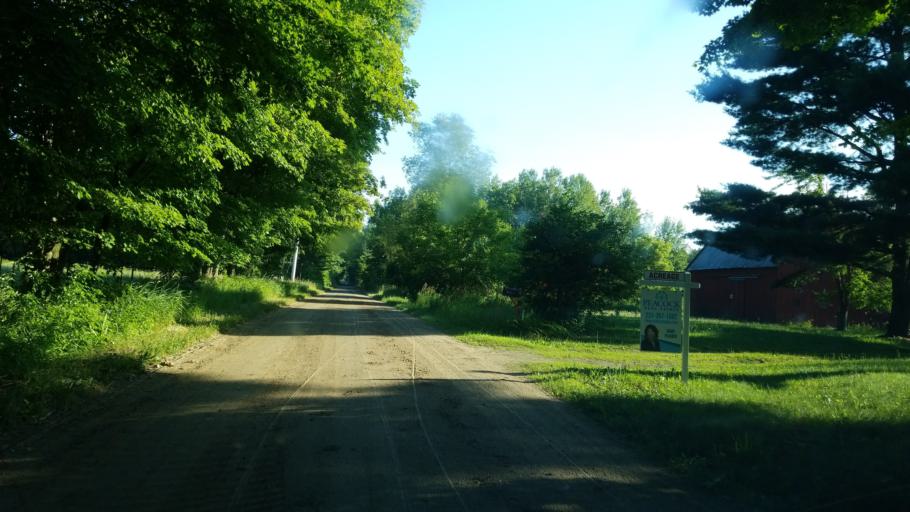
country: US
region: Michigan
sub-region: Mecosta County
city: Canadian Lakes
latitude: 43.5434
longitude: -85.4225
